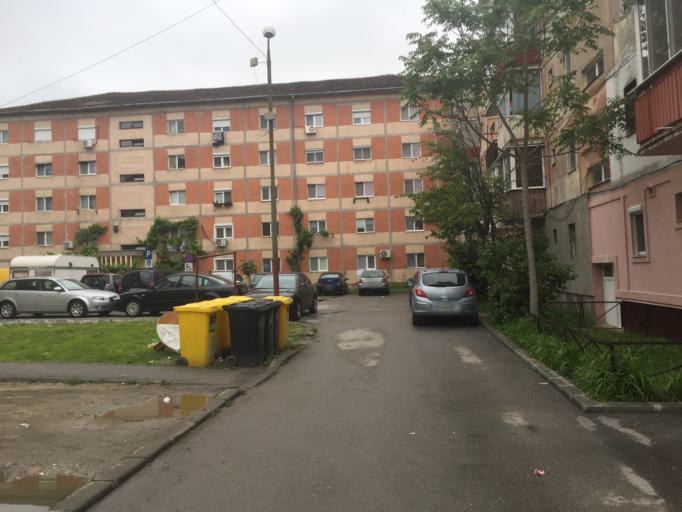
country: RO
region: Timis
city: Timisoara
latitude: 45.7541
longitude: 21.1995
